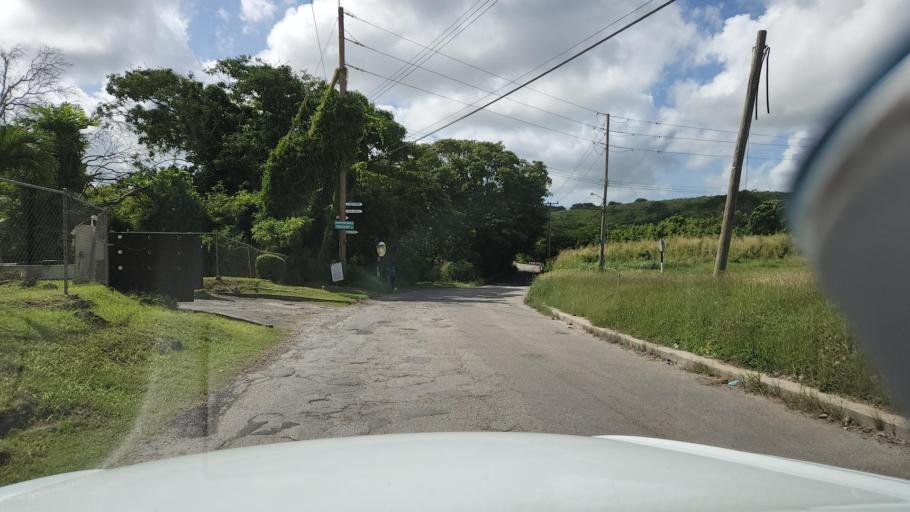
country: BB
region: Saint John
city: Four Cross Roads
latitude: 13.1441
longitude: -59.4800
